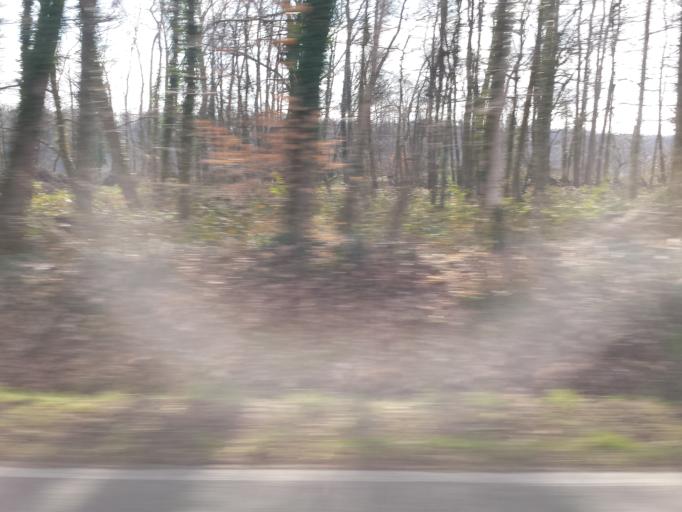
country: DE
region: North Rhine-Westphalia
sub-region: Regierungsbezirk Munster
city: Havixbeck
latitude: 51.9453
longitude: 7.4778
